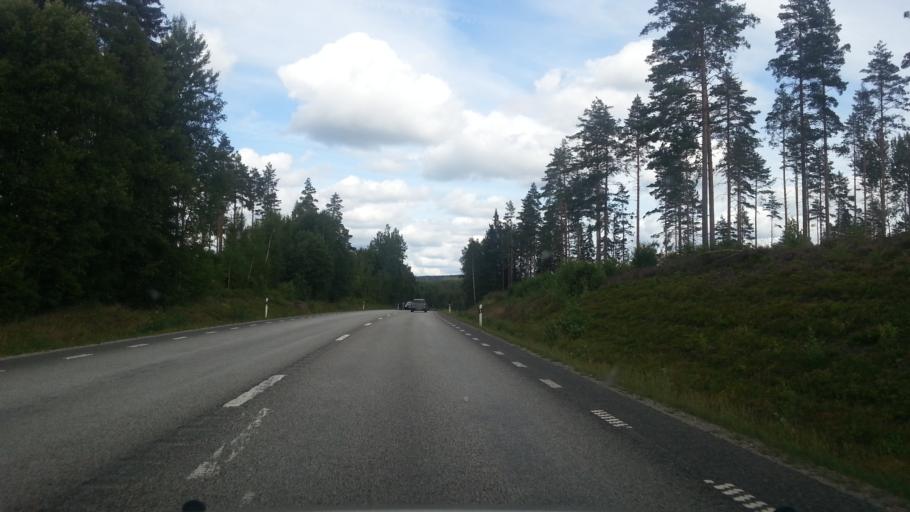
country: SE
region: OErebro
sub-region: Lindesbergs Kommun
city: Lindesberg
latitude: 59.6540
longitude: 15.2487
